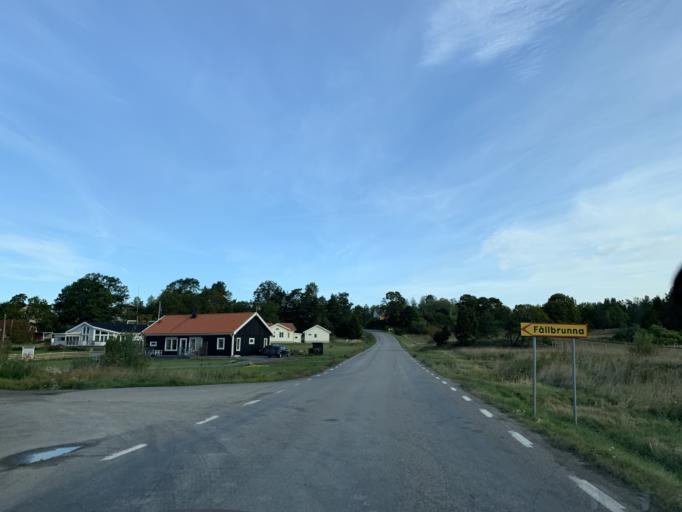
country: SE
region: Stockholm
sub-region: Haninge Kommun
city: Jordbro
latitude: 59.0633
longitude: 18.0667
